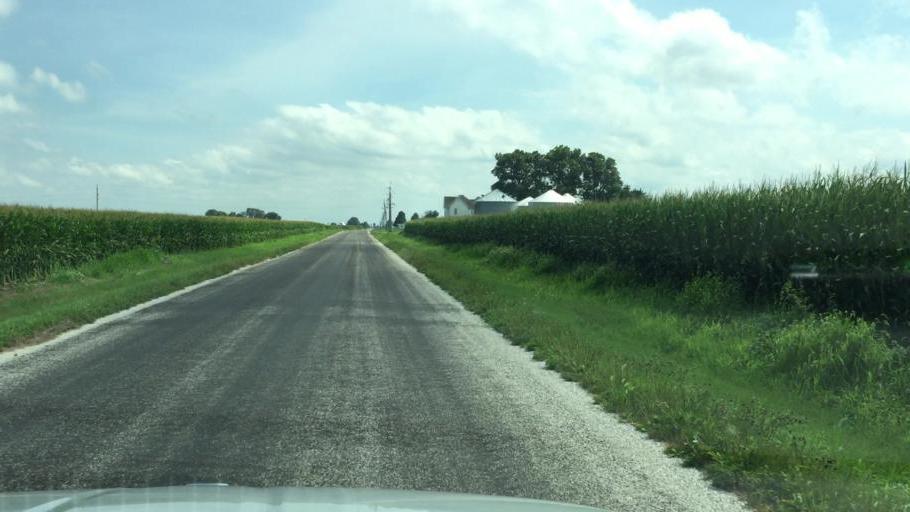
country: US
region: Illinois
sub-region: Hancock County
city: Carthage
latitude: 40.5234
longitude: -91.1771
